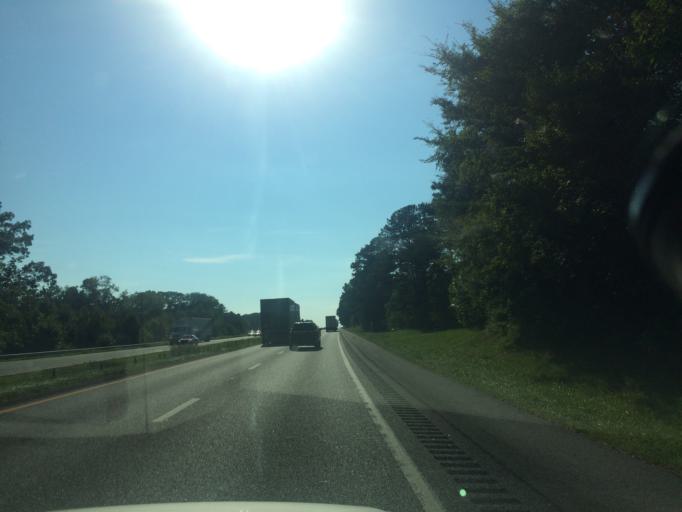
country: US
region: South Carolina
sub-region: Cherokee County
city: East Gaffney
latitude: 35.1106
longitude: -81.5887
